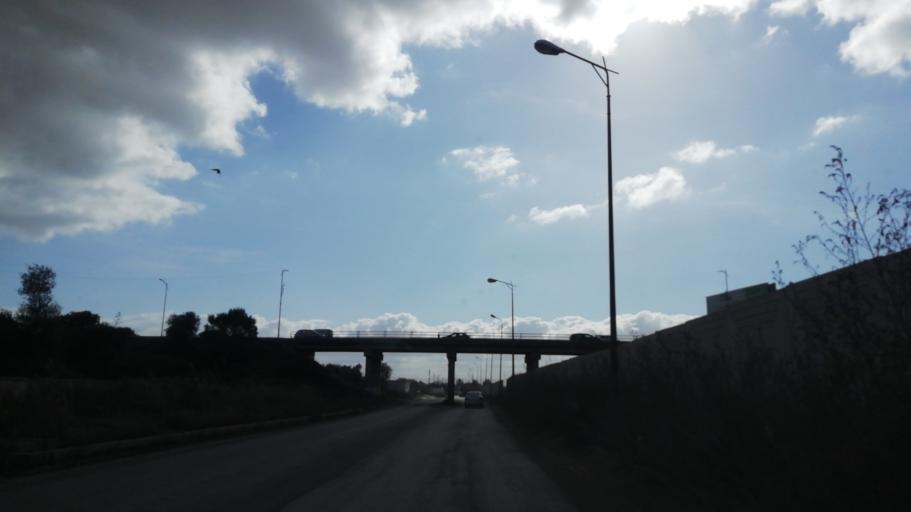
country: DZ
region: Oran
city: Es Senia
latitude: 35.6246
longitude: -0.5896
